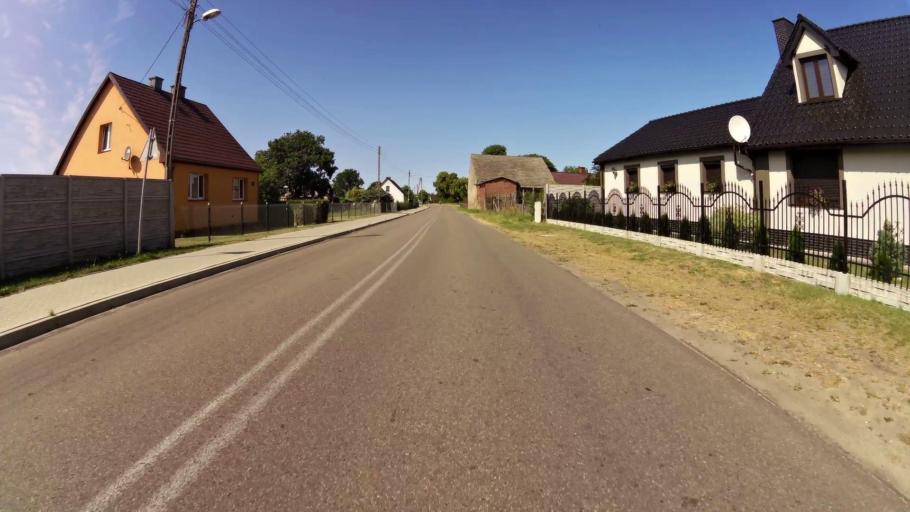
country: PL
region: West Pomeranian Voivodeship
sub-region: Powiat stargardzki
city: Dobrzany
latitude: 53.3421
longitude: 15.3955
